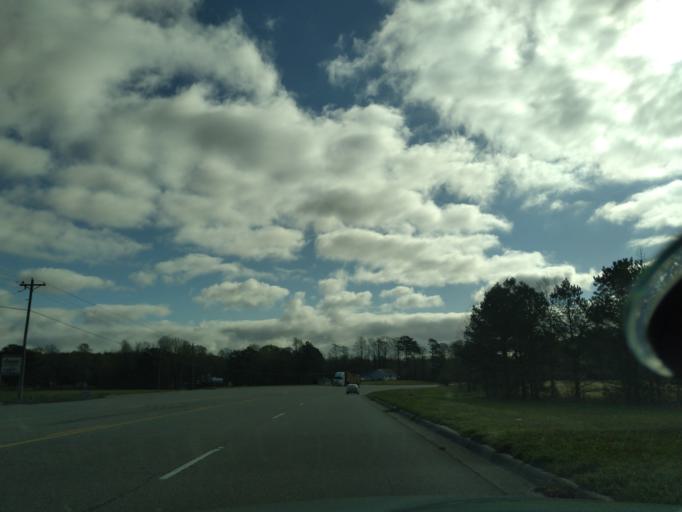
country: US
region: North Carolina
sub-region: Chowan County
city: Edenton
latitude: 36.0376
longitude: -76.7709
